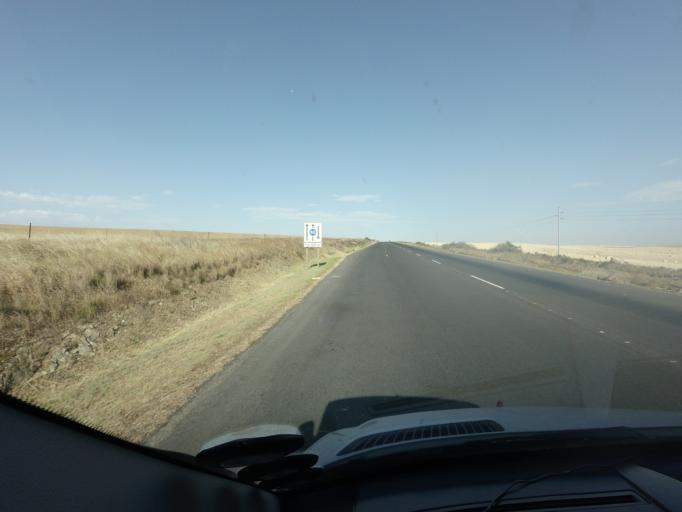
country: ZA
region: Western Cape
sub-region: Cape Winelands District Municipality
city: Ashton
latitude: -34.1577
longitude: 19.9544
